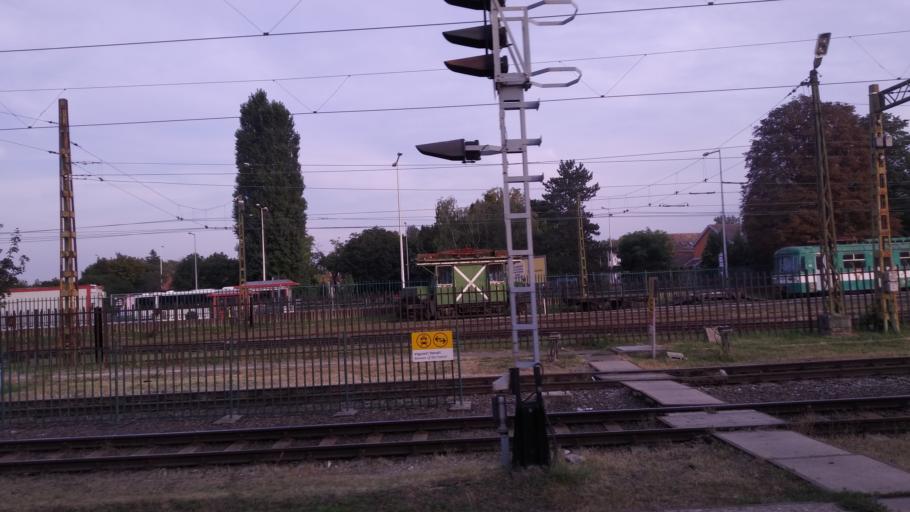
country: HU
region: Pest
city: Szentendre
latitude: 47.6602
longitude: 19.0743
